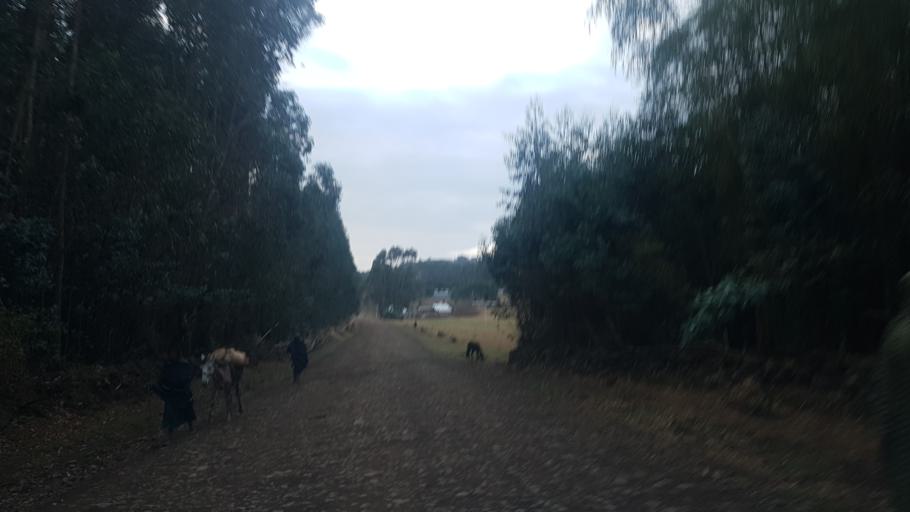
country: ET
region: Amhara
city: Finote Selam
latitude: 10.8172
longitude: 37.6435
